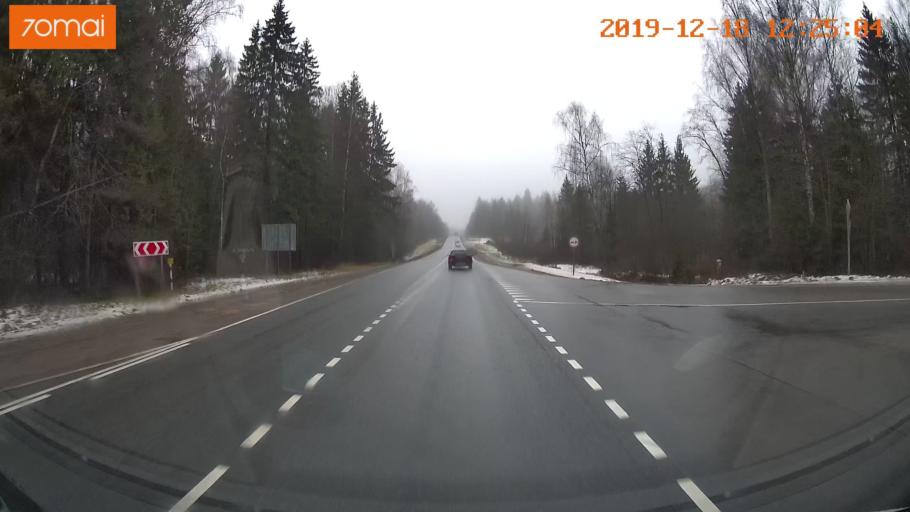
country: RU
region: Moskovskaya
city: Novopetrovskoye
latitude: 56.0331
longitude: 36.5001
